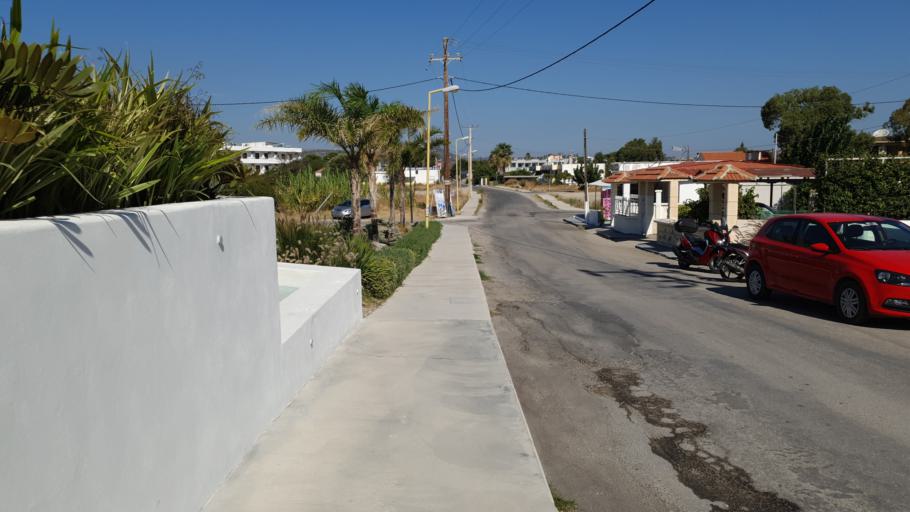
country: GR
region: South Aegean
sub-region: Nomos Dodekanisou
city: Faliraki
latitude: 36.3313
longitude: 28.2073
